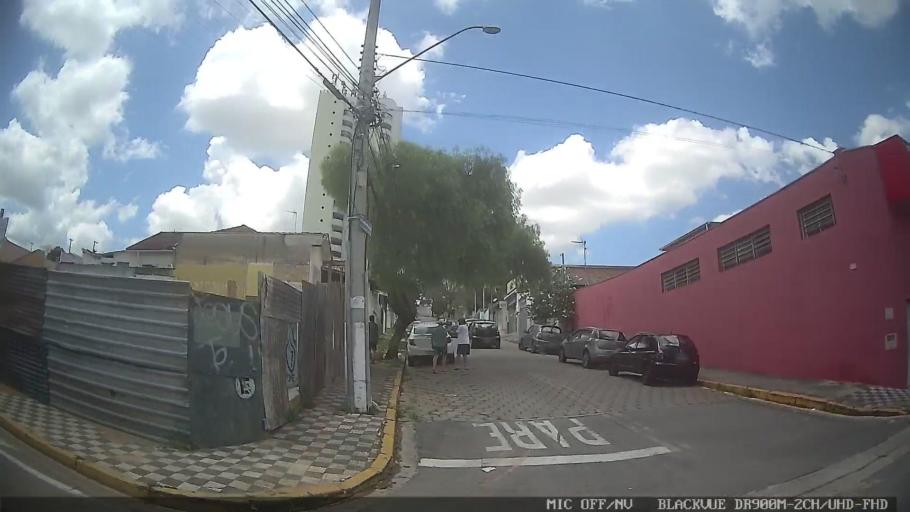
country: BR
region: Sao Paulo
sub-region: Jacarei
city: Jacarei
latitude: -23.3011
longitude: -45.9570
